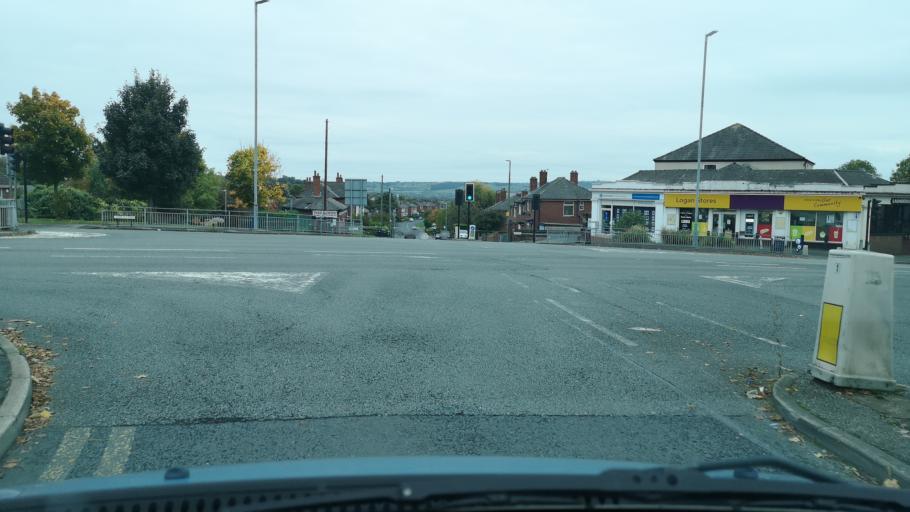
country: GB
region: England
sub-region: Kirklees
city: Heckmondwike
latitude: 53.7157
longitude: -1.6796
